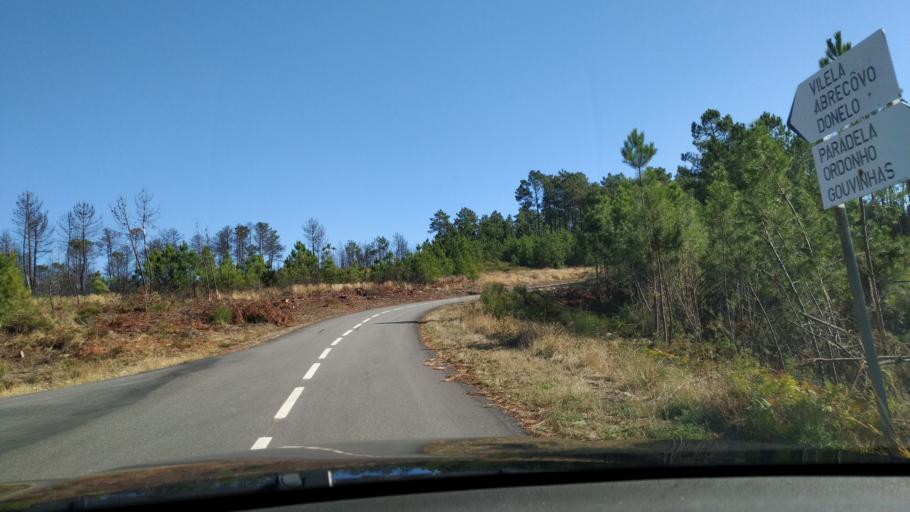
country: PT
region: Vila Real
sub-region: Sabrosa
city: Vilela
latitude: 41.2296
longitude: -7.6225
